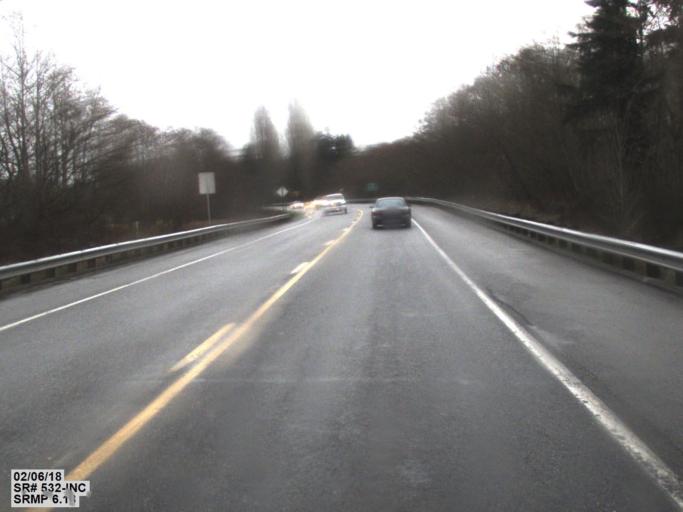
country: US
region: Washington
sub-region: Snohomish County
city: Stanwood
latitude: 48.2382
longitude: -122.3247
